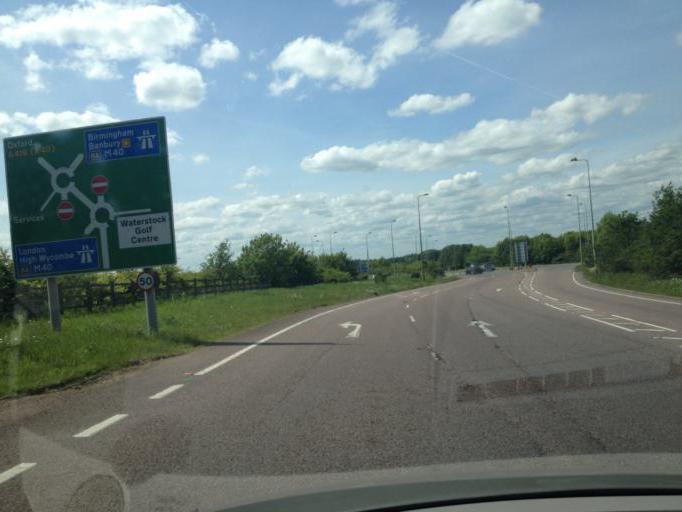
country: GB
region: England
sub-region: Oxfordshire
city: Wheatley
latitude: 51.7392
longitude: -1.0926
